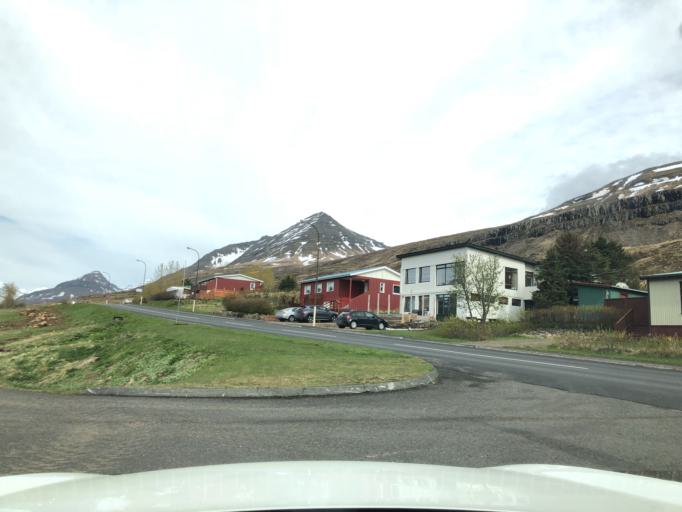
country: IS
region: East
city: Eskifjoerdur
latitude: 64.8352
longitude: -13.8812
